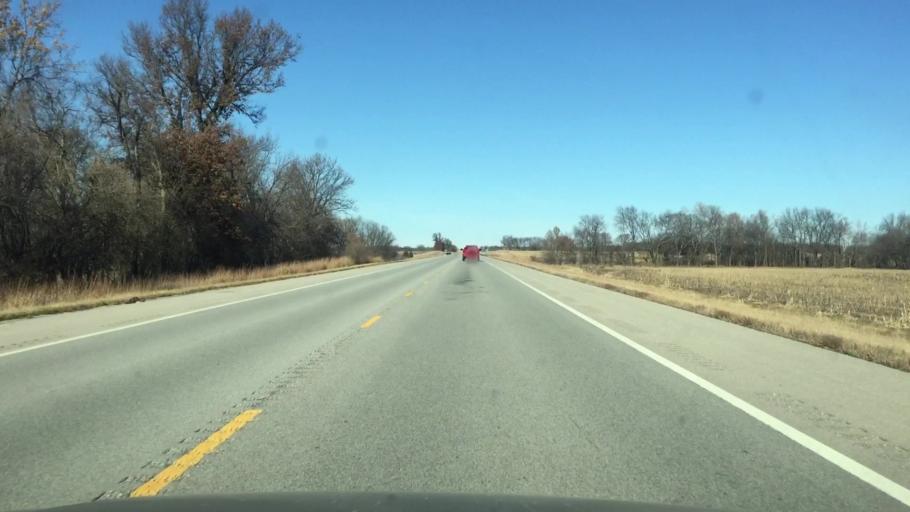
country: US
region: Kansas
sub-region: Allen County
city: Iola
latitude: 37.9827
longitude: -95.3810
